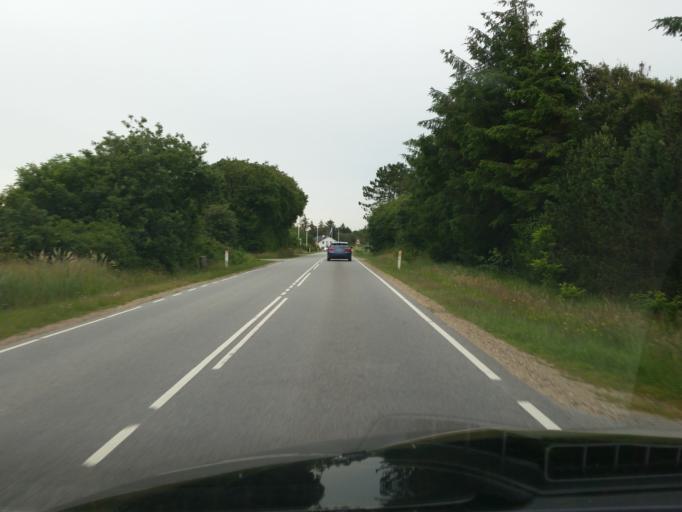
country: DK
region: South Denmark
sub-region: Varde Kommune
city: Oksbol
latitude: 55.8046
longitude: 8.2244
